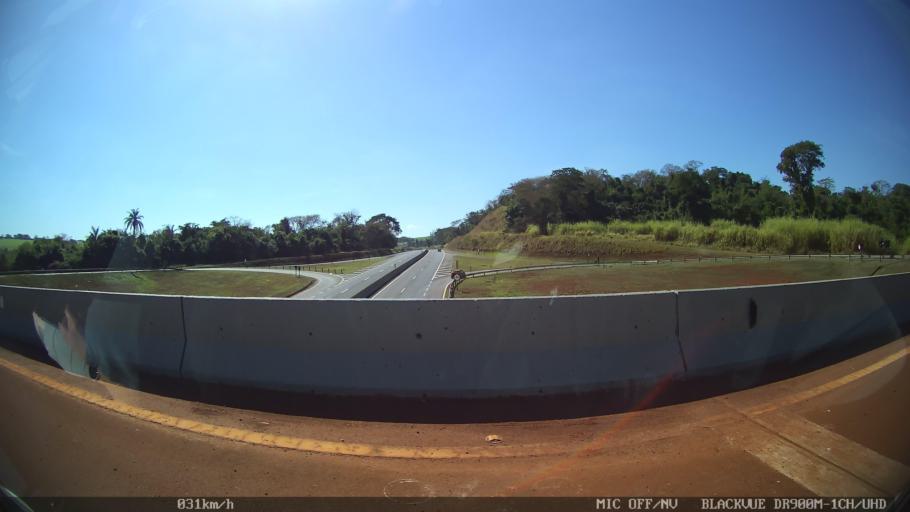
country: BR
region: Sao Paulo
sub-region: Franca
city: Franca
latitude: -20.6345
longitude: -47.4690
